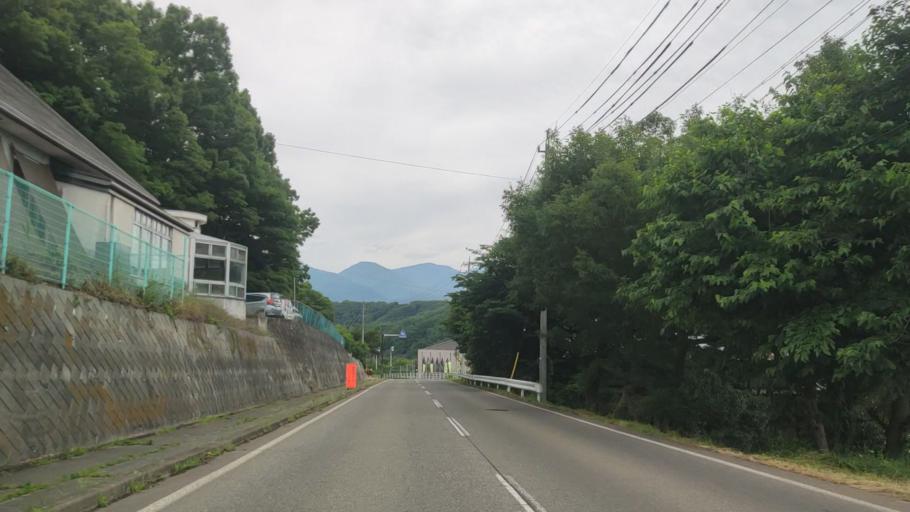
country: JP
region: Nagano
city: Kamimaruko
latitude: 36.3249
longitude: 138.3402
